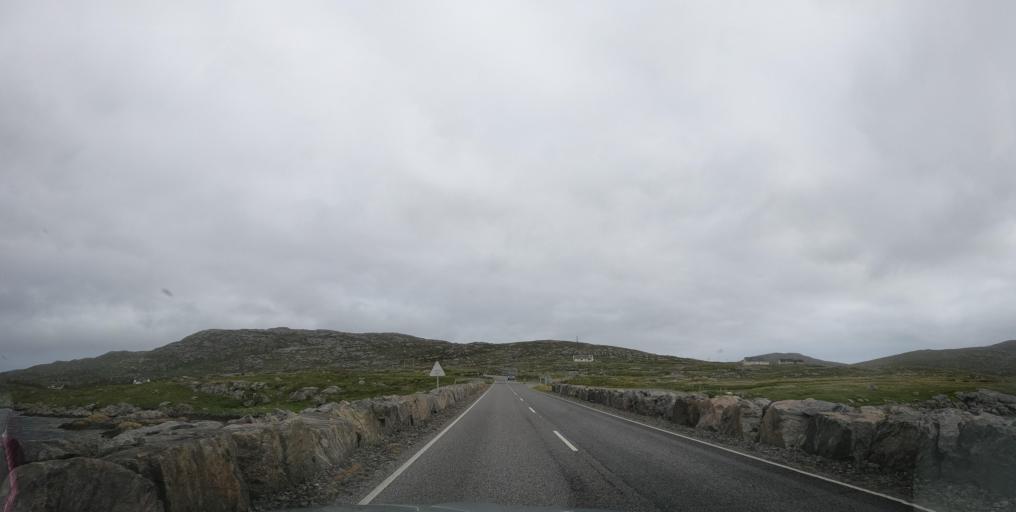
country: GB
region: Scotland
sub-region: Eilean Siar
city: Isle of South Uist
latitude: 57.1025
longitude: -7.3181
